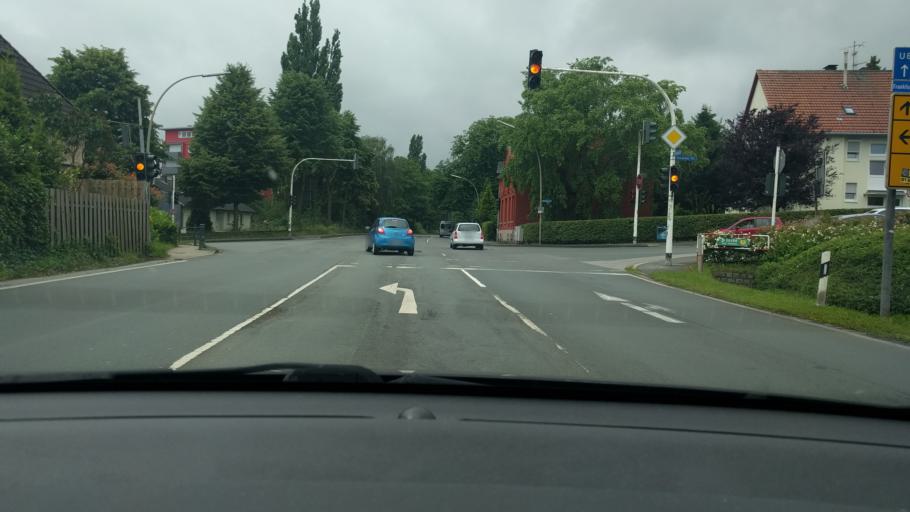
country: DE
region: North Rhine-Westphalia
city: Witten
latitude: 51.4551
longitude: 7.3751
